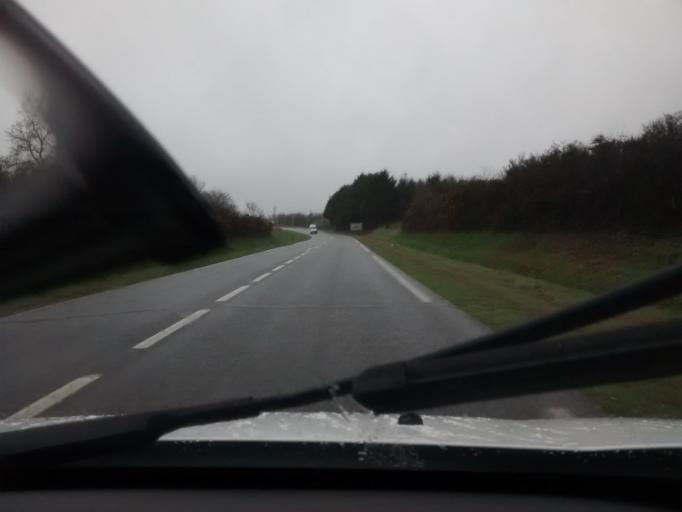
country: FR
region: Brittany
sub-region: Departement d'Ille-et-Vilaine
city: Acigne
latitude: 48.1260
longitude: -1.5279
